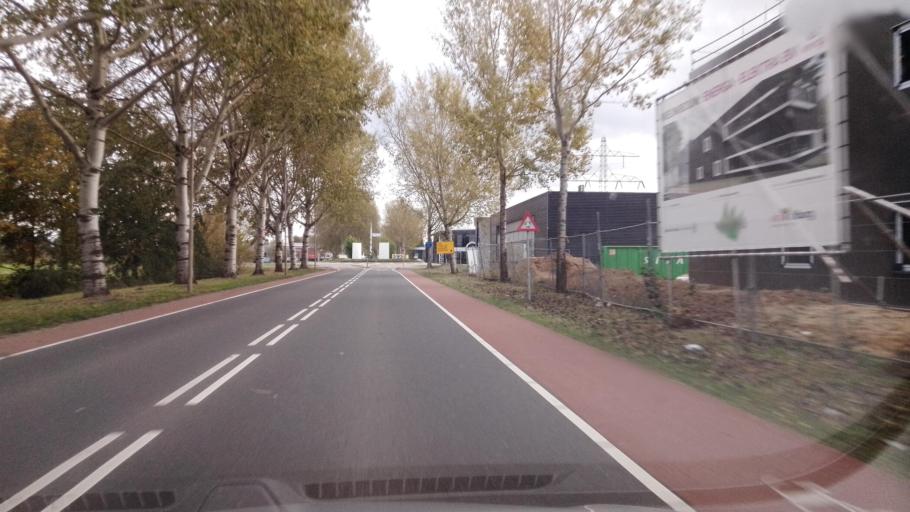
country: NL
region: Limburg
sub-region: Gemeente Venlo
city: Venlo
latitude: 51.3804
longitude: 6.1513
